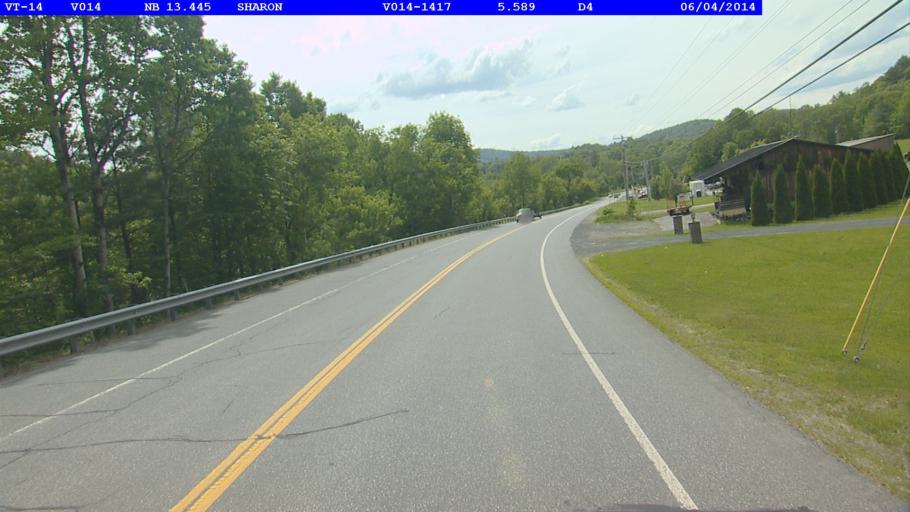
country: US
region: Vermont
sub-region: Windsor County
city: Woodstock
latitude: 43.7808
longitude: -72.4641
